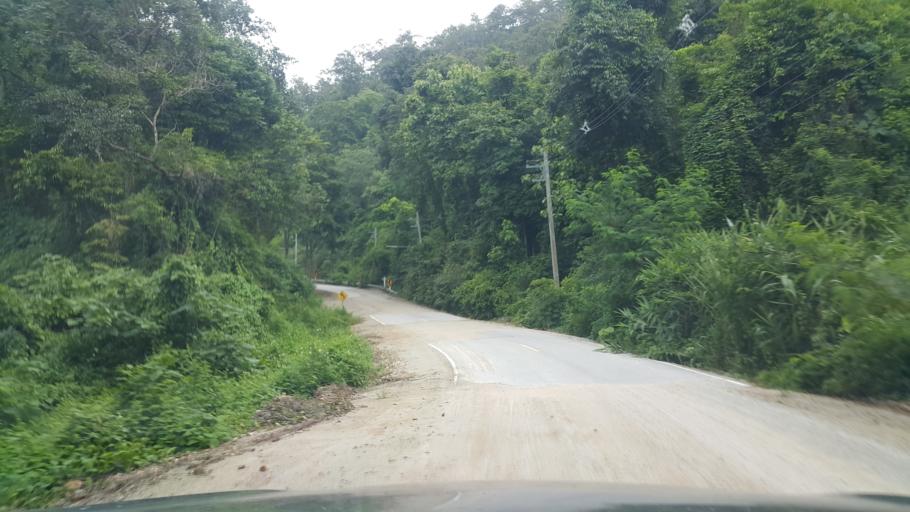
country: TH
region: Chiang Mai
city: San Sai
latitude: 18.9748
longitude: 99.1229
